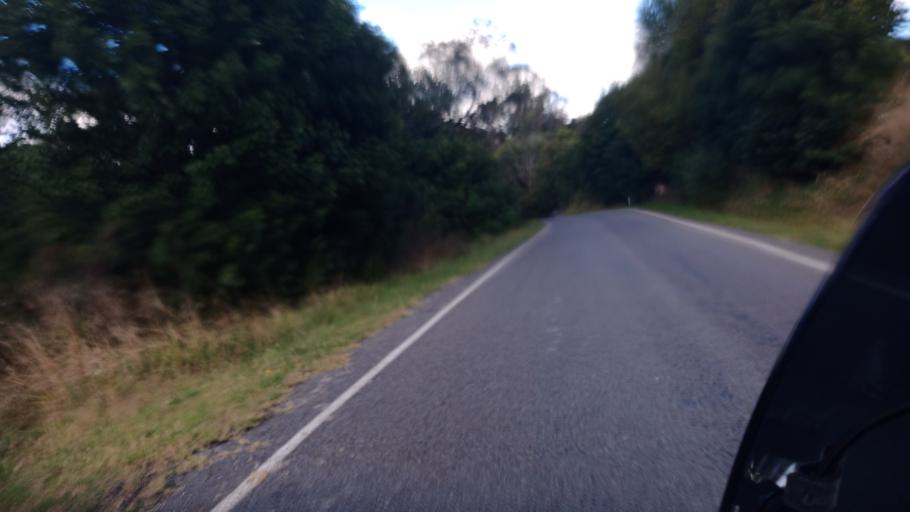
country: NZ
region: Gisborne
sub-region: Gisborne District
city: Gisborne
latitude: -38.5310
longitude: 177.5390
